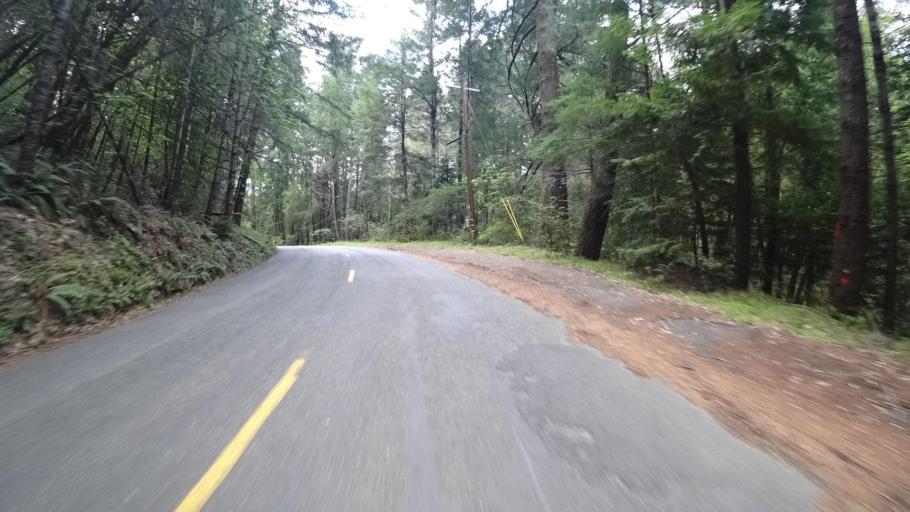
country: US
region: California
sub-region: Humboldt County
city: Redway
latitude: 40.0065
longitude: -123.9292
